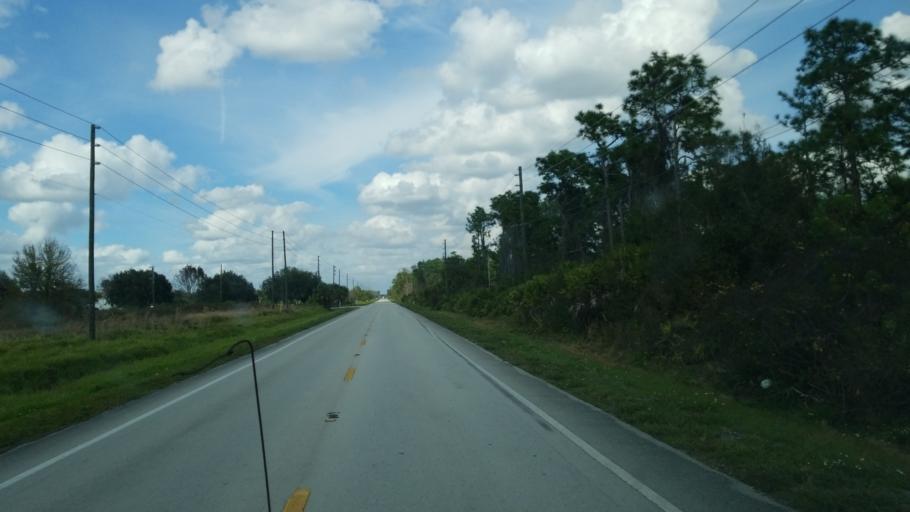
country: US
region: Florida
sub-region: Osceola County
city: Saint Cloud
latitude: 28.1140
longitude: -81.0763
